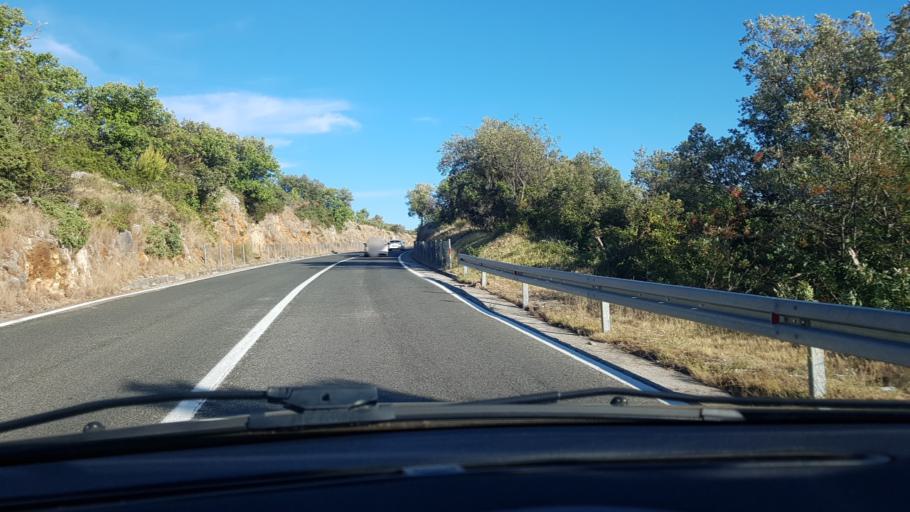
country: HR
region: Sibensko-Kniniska
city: Primosten
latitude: 43.5807
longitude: 15.9366
